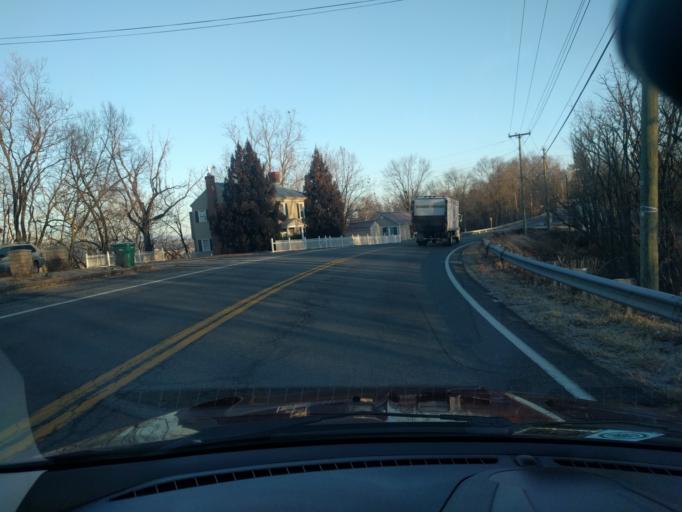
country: US
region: Virginia
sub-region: Rockingham County
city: Bridgewater
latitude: 38.3521
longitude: -78.9450
